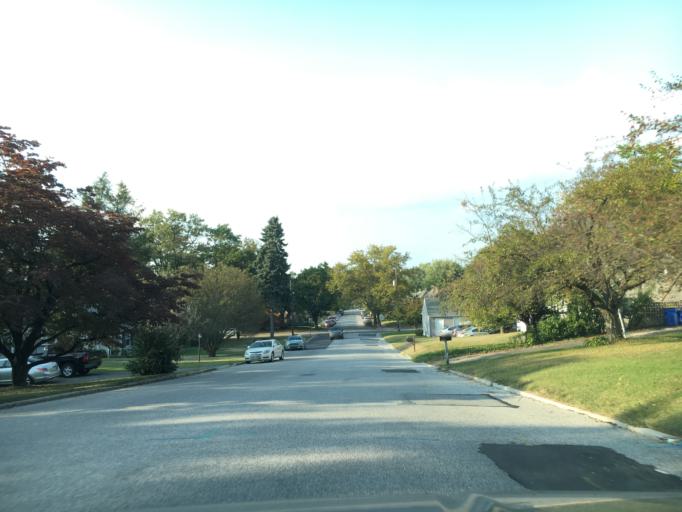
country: US
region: Pennsylvania
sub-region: York County
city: Valley View
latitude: 39.9542
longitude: -76.6995
